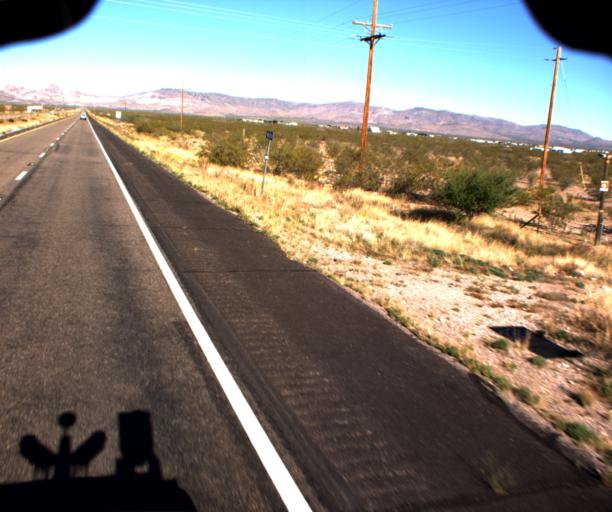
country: US
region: Arizona
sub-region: Mohave County
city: Golden Valley
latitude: 35.2259
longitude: -114.2933
